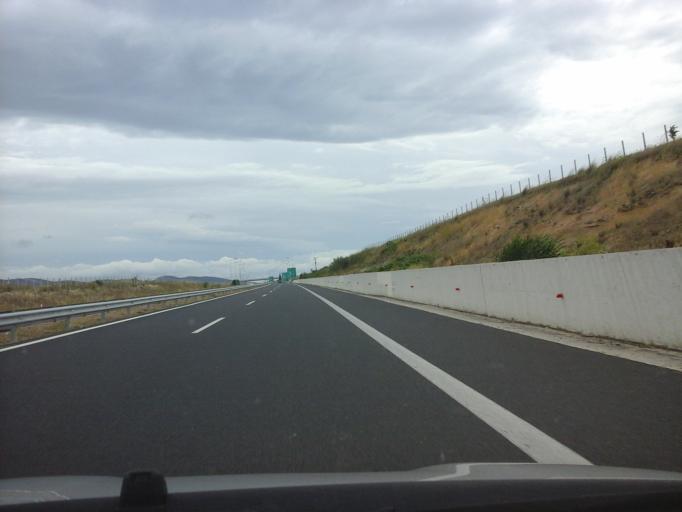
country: GR
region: East Macedonia and Thrace
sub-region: Nomos Evrou
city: Alexandroupoli
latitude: 40.9040
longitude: 25.9361
